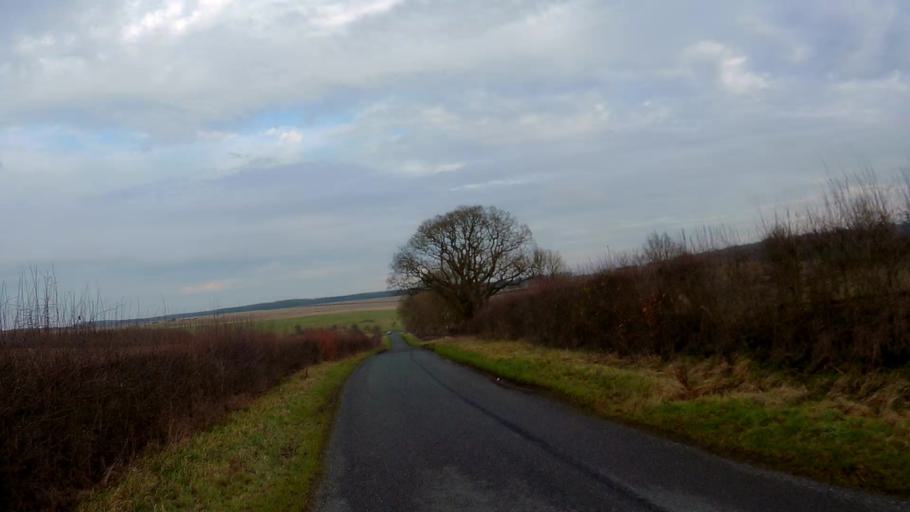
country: GB
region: England
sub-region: Lincolnshire
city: Bourne
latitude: 52.8321
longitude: -0.4666
